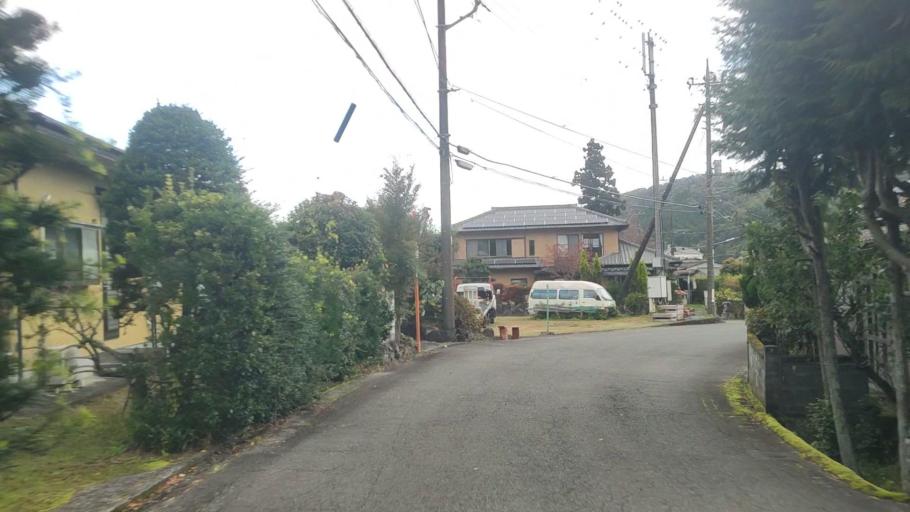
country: JP
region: Shizuoka
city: Ito
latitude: 34.9284
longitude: 139.0005
